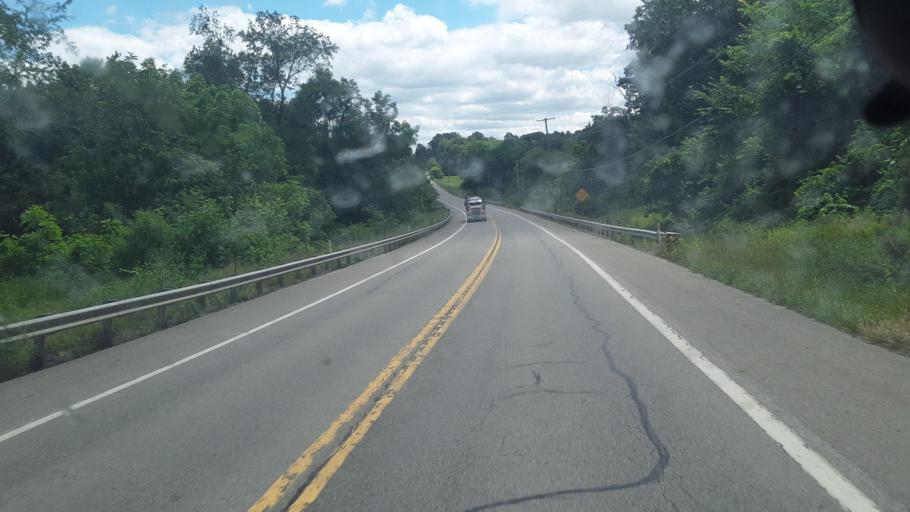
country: US
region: Pennsylvania
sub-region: Butler County
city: Slippery Rock
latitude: 40.9846
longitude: -80.1708
